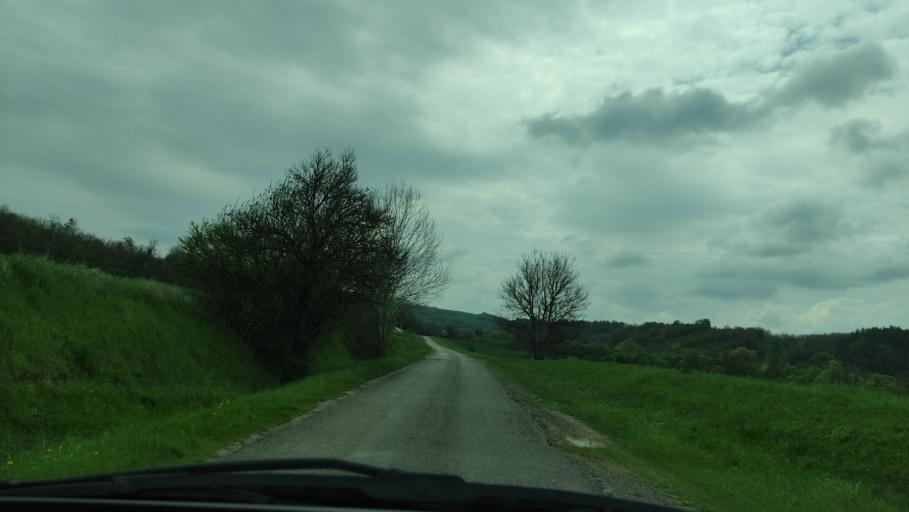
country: HU
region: Baranya
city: Magocs
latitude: 46.3026
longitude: 18.1929
